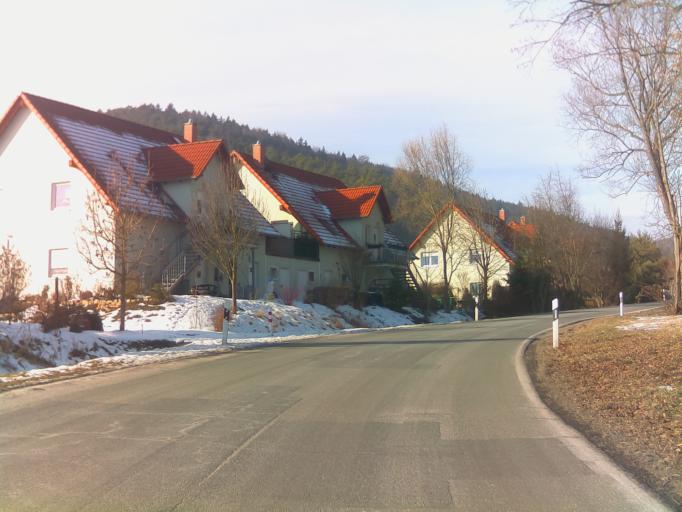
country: DE
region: Thuringia
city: Altenberga
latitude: 50.8451
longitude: 11.5523
